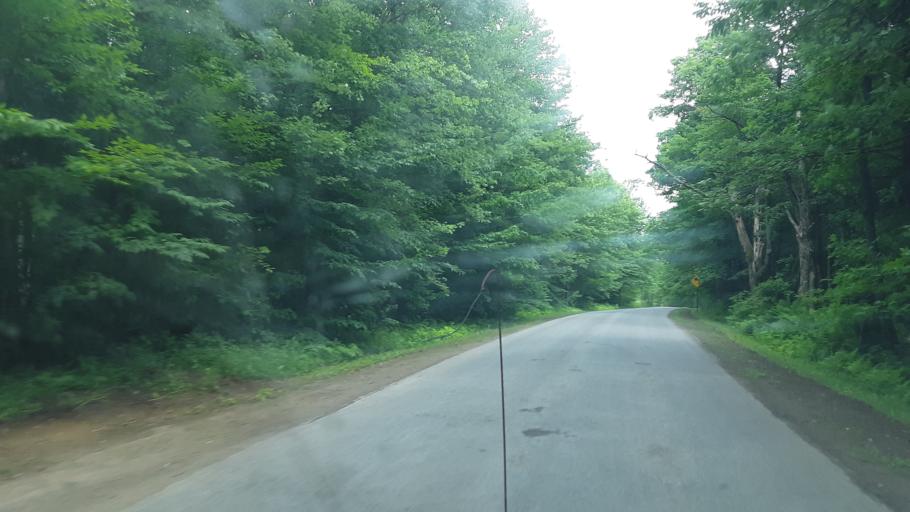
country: US
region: New York
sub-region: Oneida County
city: Rome
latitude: 43.3954
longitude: -75.5230
